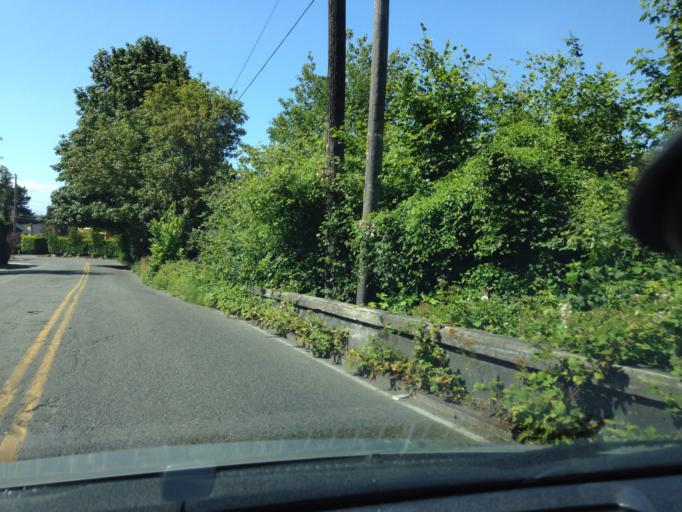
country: US
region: Washington
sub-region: King County
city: Seattle
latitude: 47.6376
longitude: -122.3138
